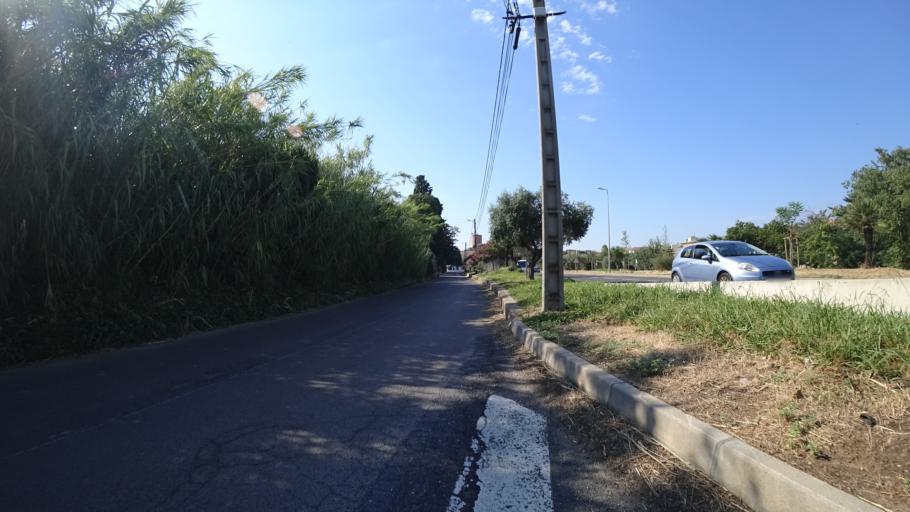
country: FR
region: Languedoc-Roussillon
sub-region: Departement des Pyrenees-Orientales
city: Perpignan
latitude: 42.7043
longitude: 2.9093
